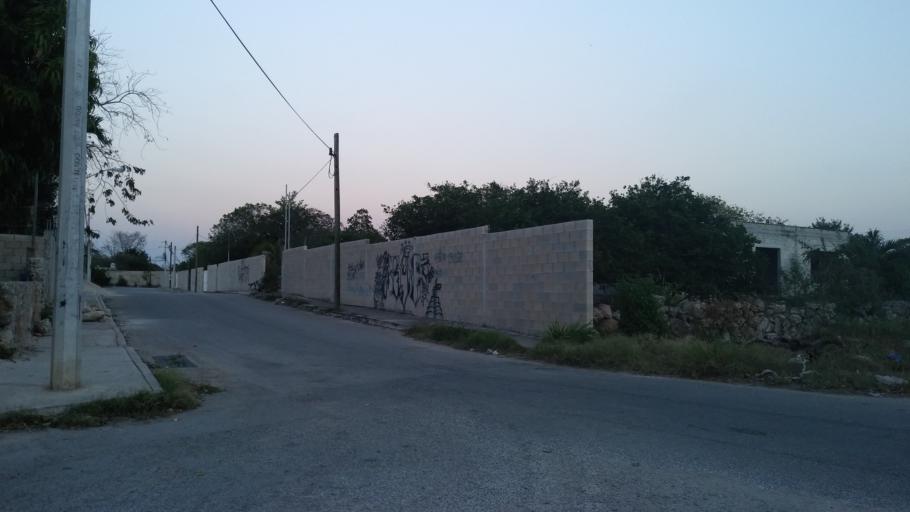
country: MX
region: Yucatan
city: Itzincab Palomeque
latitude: 20.9281
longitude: -89.6703
